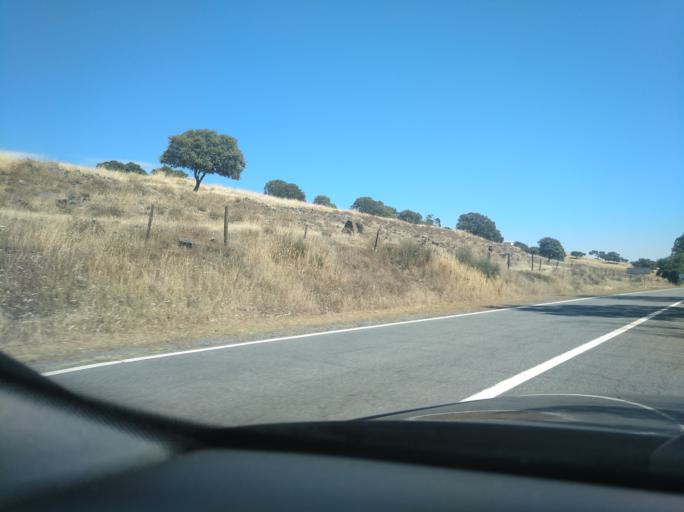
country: PT
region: Beja
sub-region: Castro Verde
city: Castro Verde
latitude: 37.6790
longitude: -8.0833
